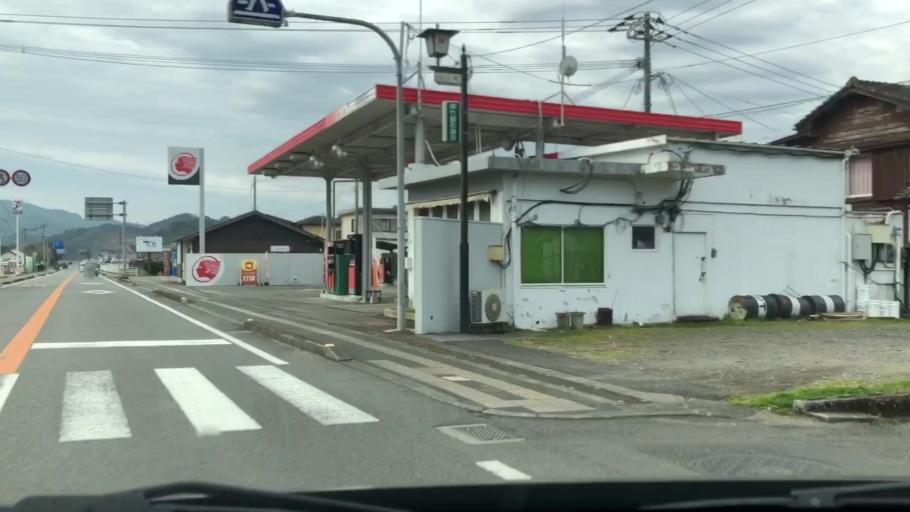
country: JP
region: Oita
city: Saiki
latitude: 32.9678
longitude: 131.8382
